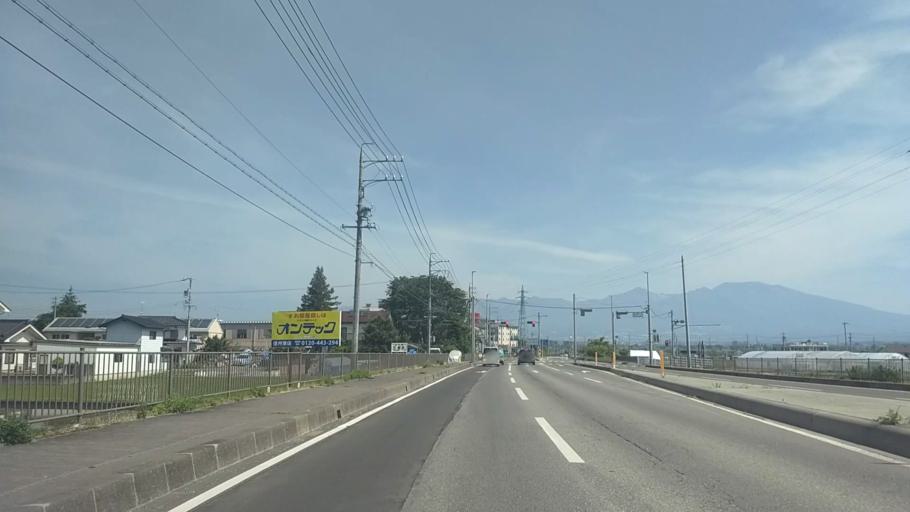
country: JP
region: Nagano
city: Saku
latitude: 36.2278
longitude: 138.4562
